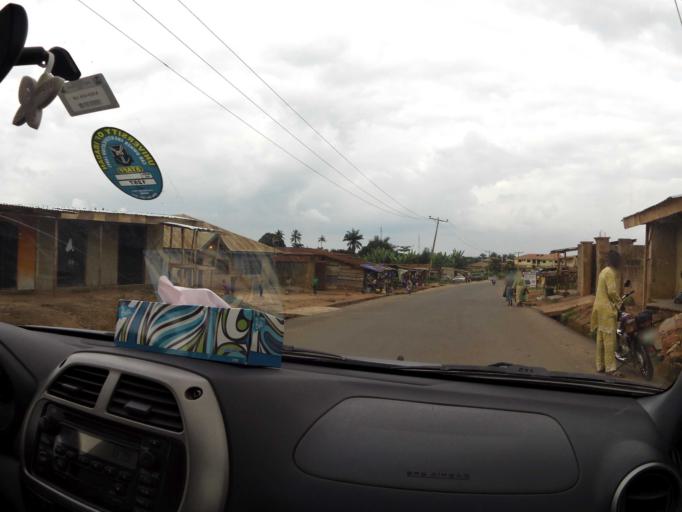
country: NG
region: Oyo
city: Moniya
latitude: 7.5258
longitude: 3.9208
